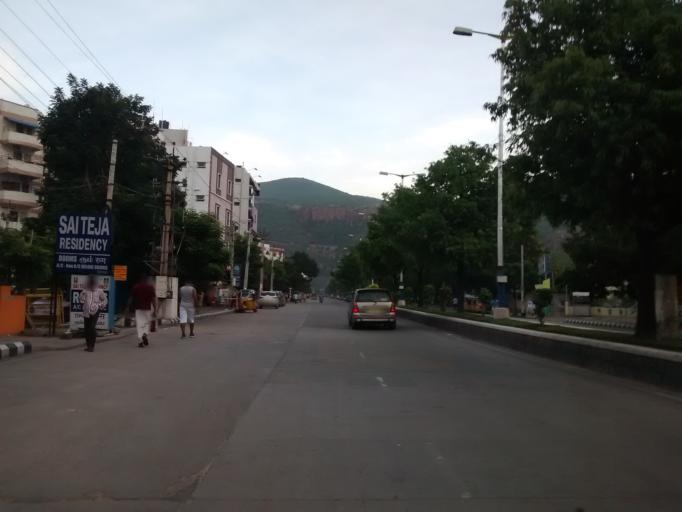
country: IN
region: Andhra Pradesh
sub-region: Chittoor
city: Akkarampalle
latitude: 13.6487
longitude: 79.4252
